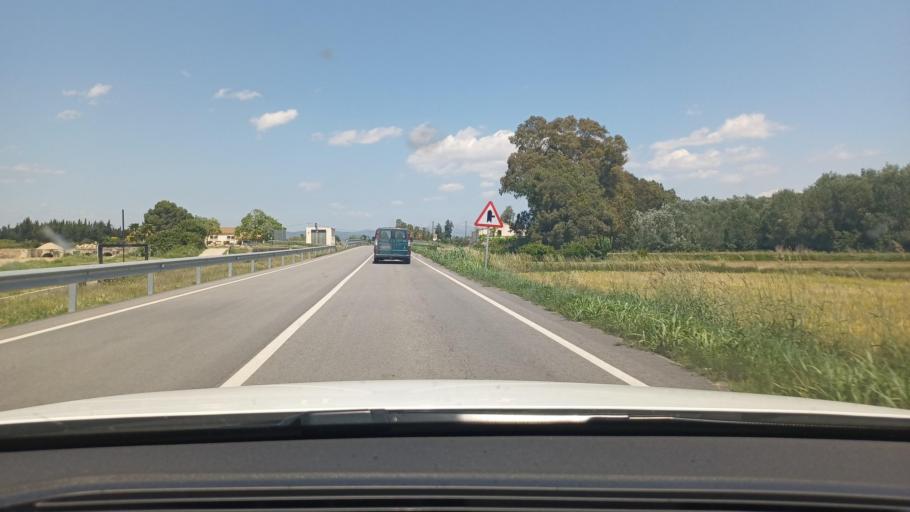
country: ES
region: Catalonia
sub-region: Provincia de Tarragona
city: Amposta
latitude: 40.6693
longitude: 0.5907
